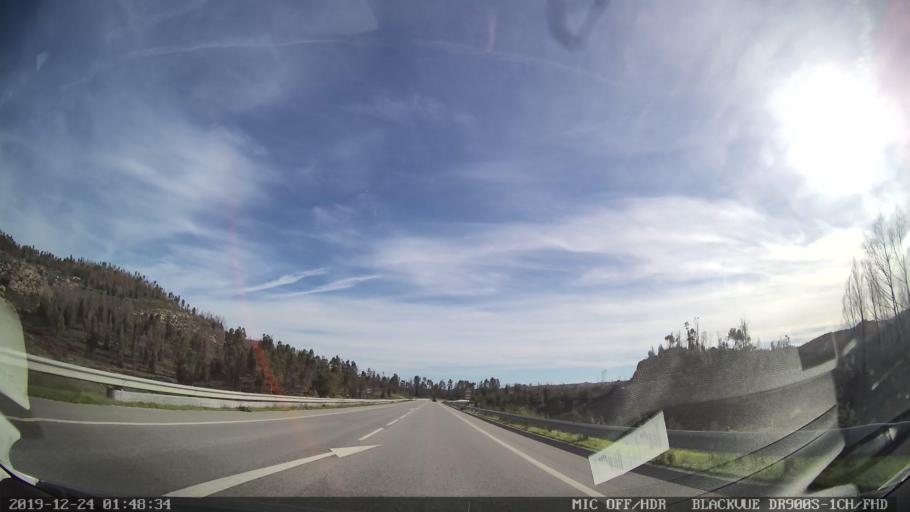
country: PT
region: Portalegre
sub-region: Nisa
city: Nisa
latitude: 39.5202
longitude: -7.7742
